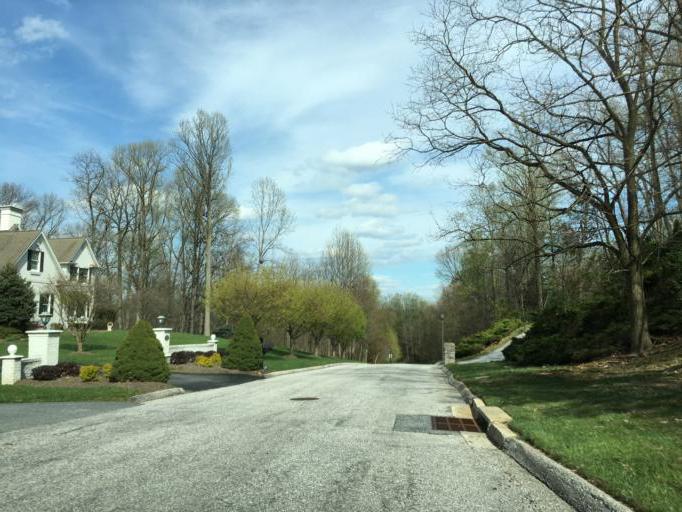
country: US
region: Maryland
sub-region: Baltimore County
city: Cockeysville
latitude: 39.4753
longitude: -76.6764
